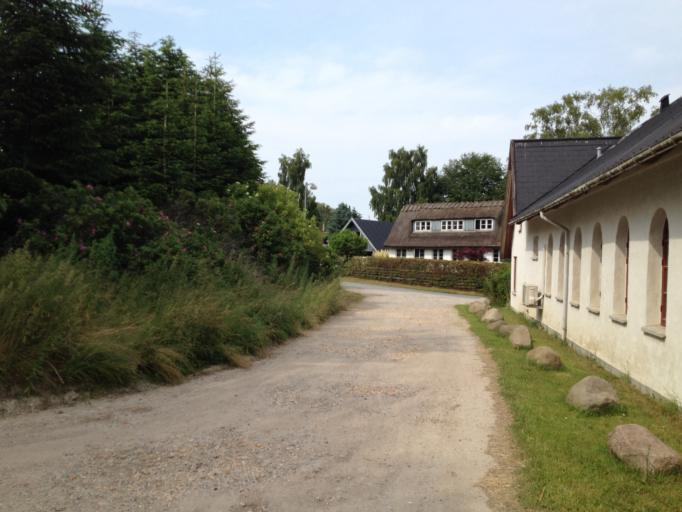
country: DK
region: Capital Region
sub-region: Fredensborg Kommune
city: Niva
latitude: 55.9516
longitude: 12.5072
